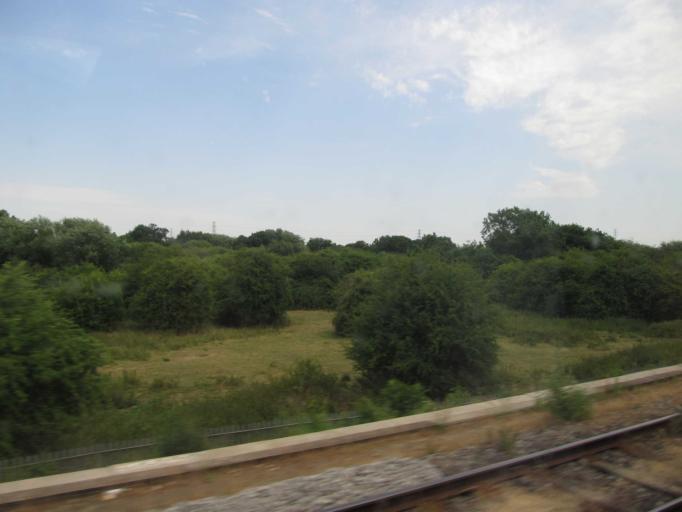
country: GB
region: England
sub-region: Surrey
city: Colnbrook
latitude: 51.5083
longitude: -0.5343
